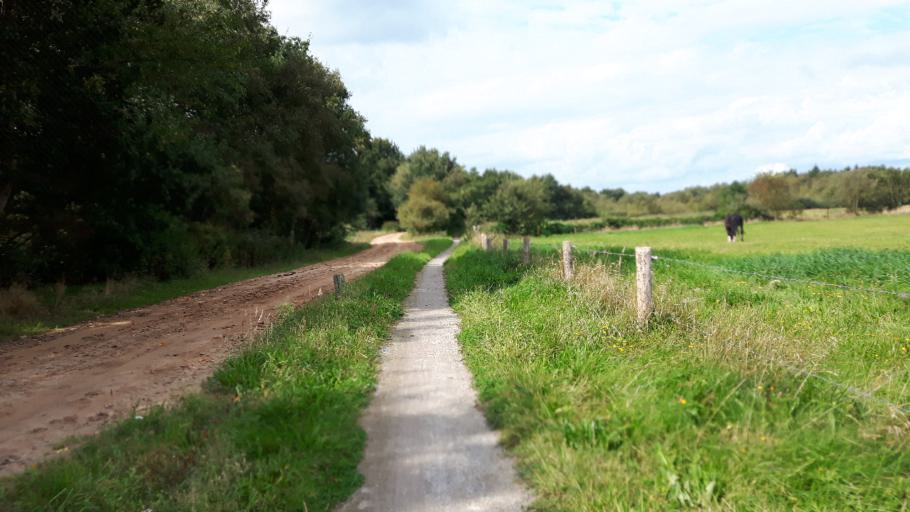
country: NL
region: Groningen
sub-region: Gemeente Leek
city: Leek
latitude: 53.1066
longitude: 6.4043
